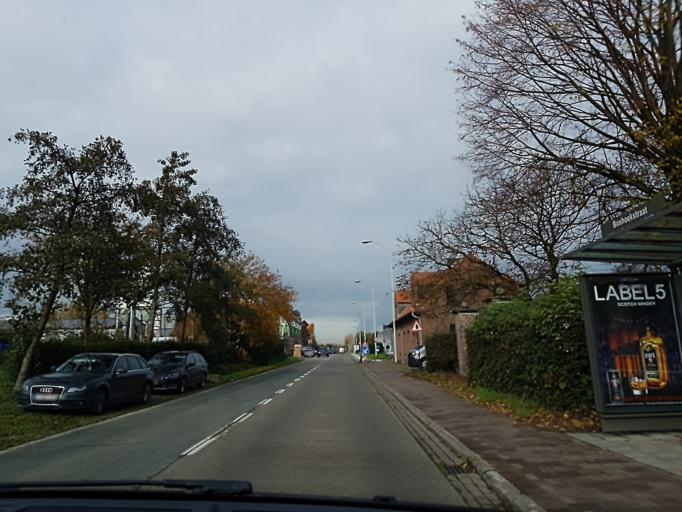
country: BE
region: Flanders
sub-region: Provincie Antwerpen
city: Lint
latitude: 51.1361
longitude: 4.4964
